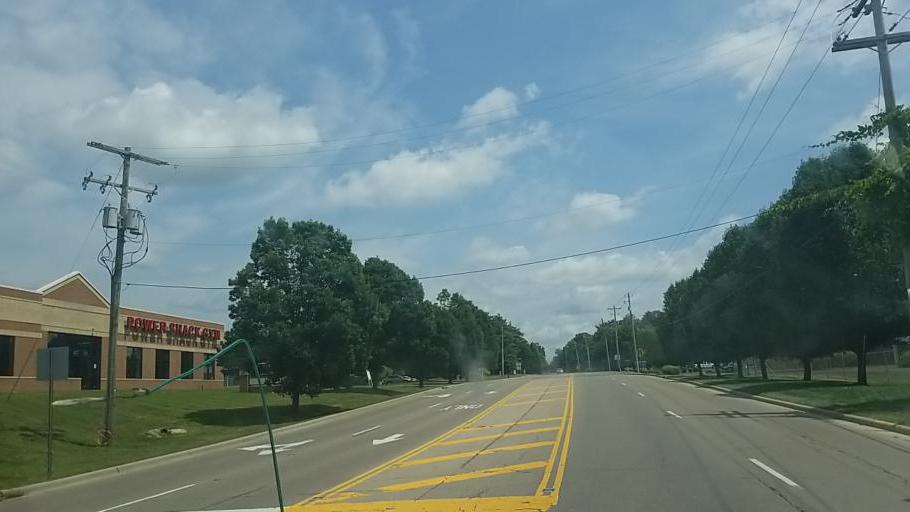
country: US
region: Ohio
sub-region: Franklin County
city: Reynoldsburg
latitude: 39.9290
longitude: -82.7835
